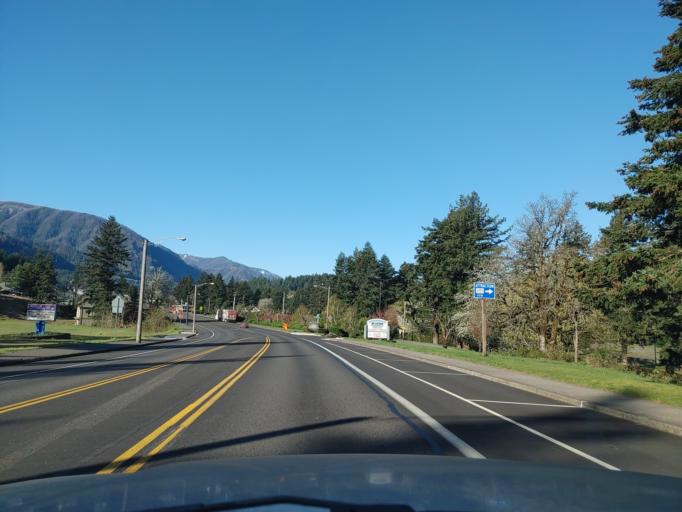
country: US
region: Oregon
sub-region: Hood River County
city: Cascade Locks
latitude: 45.6692
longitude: -121.8925
